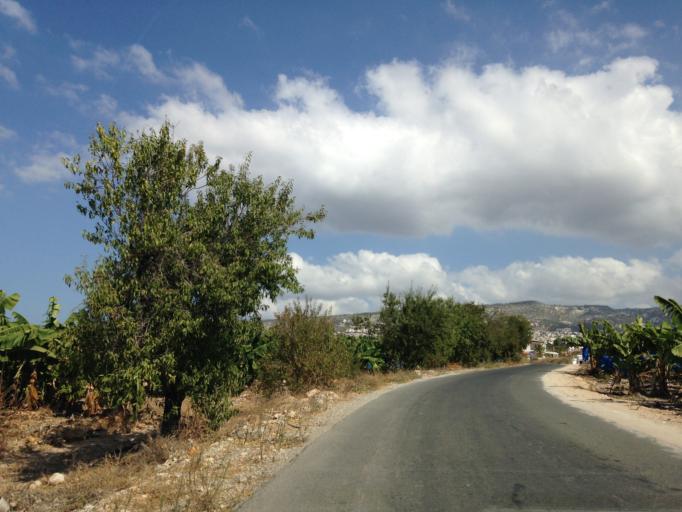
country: CY
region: Pafos
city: Pegeia
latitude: 34.8623
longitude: 32.3754
